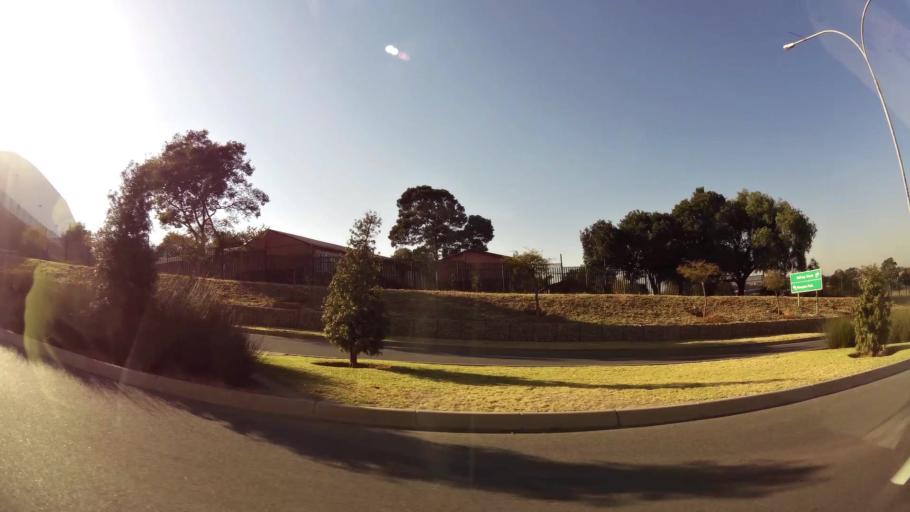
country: ZA
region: Gauteng
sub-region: City of Johannesburg Metropolitan Municipality
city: Modderfontein
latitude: -26.0562
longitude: 28.1705
